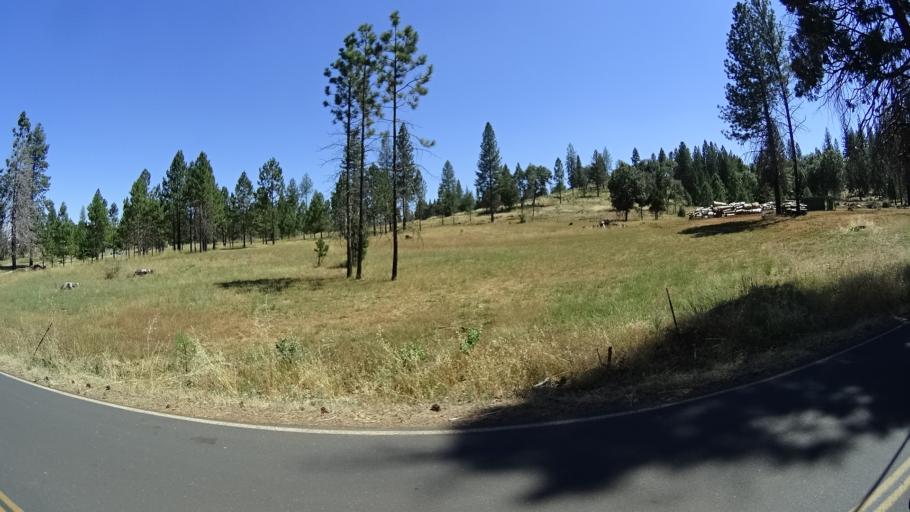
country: US
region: California
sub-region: Calaveras County
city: Mountain Ranch
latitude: 38.2815
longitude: -120.5360
